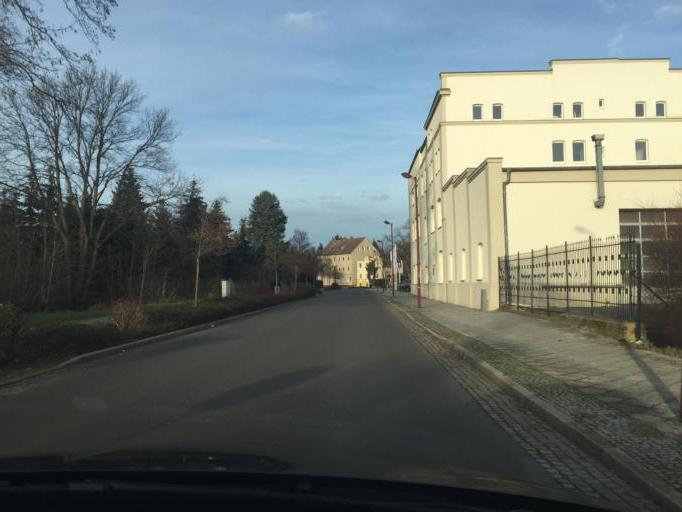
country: DE
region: Brandenburg
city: Forst
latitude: 51.7510
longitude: 14.6417
